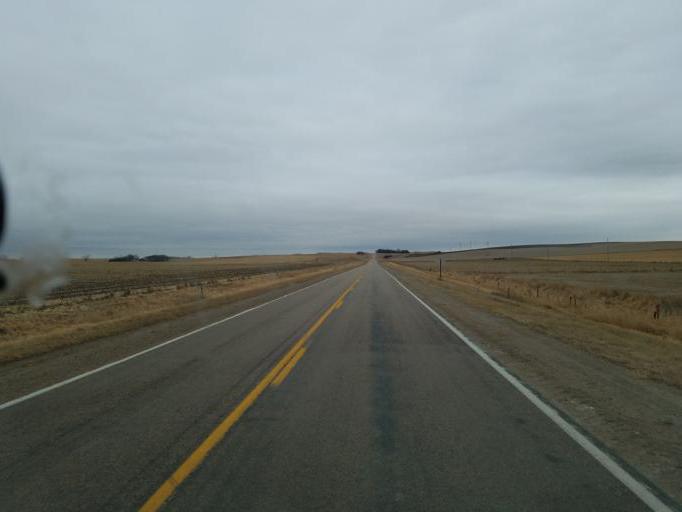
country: US
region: Nebraska
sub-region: Knox County
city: Bloomfield
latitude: 42.5976
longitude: -97.6206
